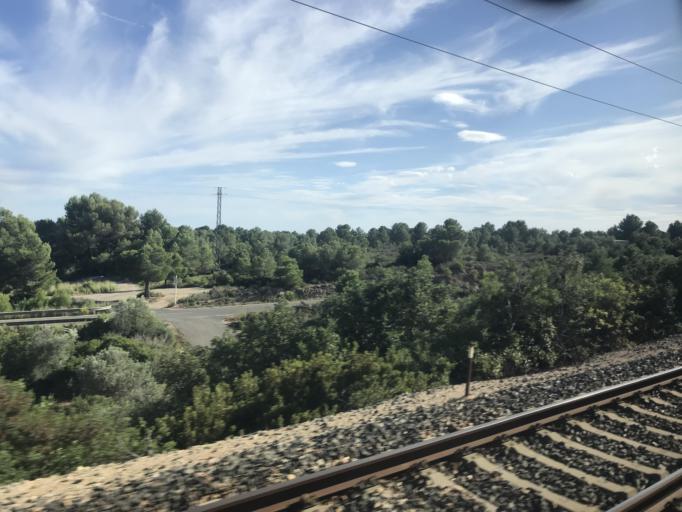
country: ES
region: Catalonia
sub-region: Provincia de Tarragona
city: l'Ametlla de Mar
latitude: 40.8736
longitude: 0.7870
